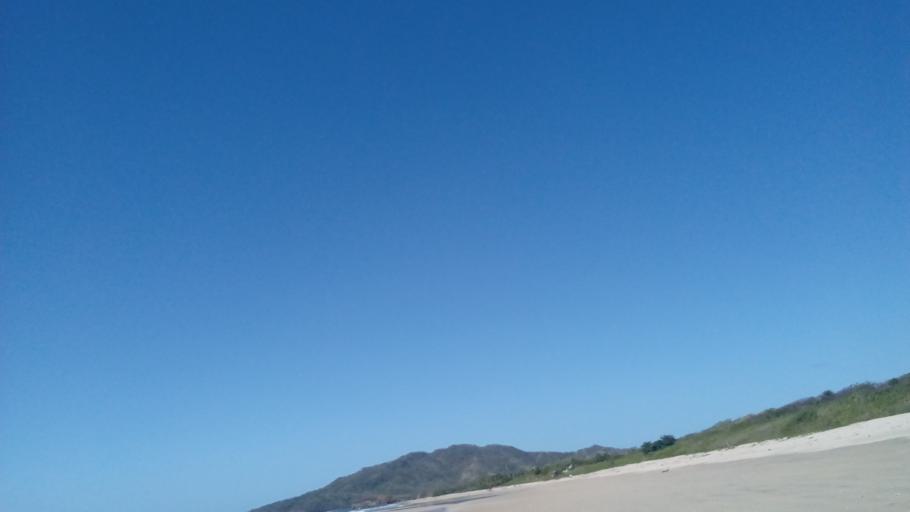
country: CR
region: Guanacaste
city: Belen
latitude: 10.3291
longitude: -85.8450
